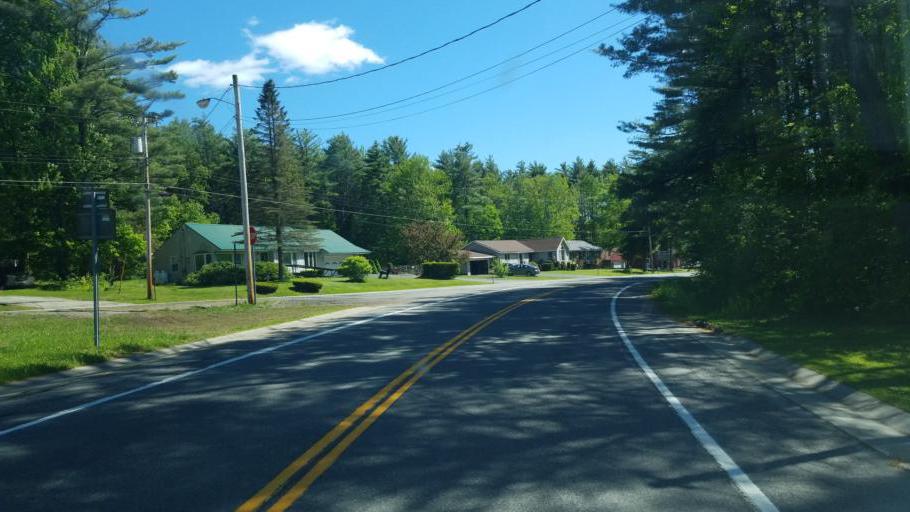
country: US
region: New York
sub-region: Fulton County
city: Gloversville
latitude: 43.1364
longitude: -74.4808
